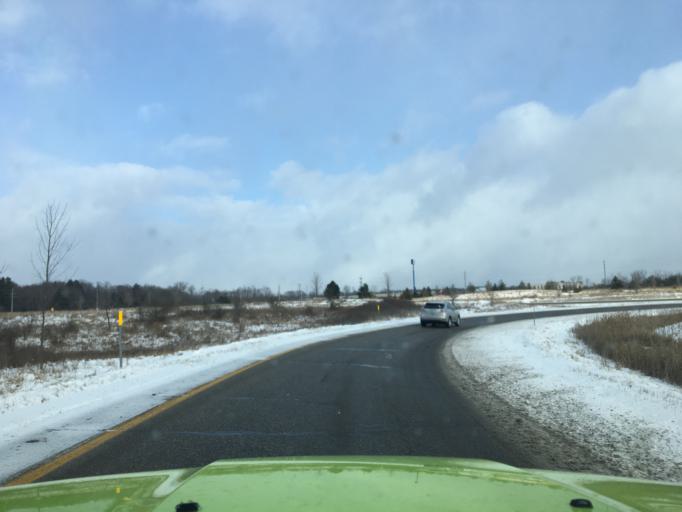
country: US
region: Michigan
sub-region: Mecosta County
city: Big Rapids
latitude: 43.6879
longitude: -85.5238
